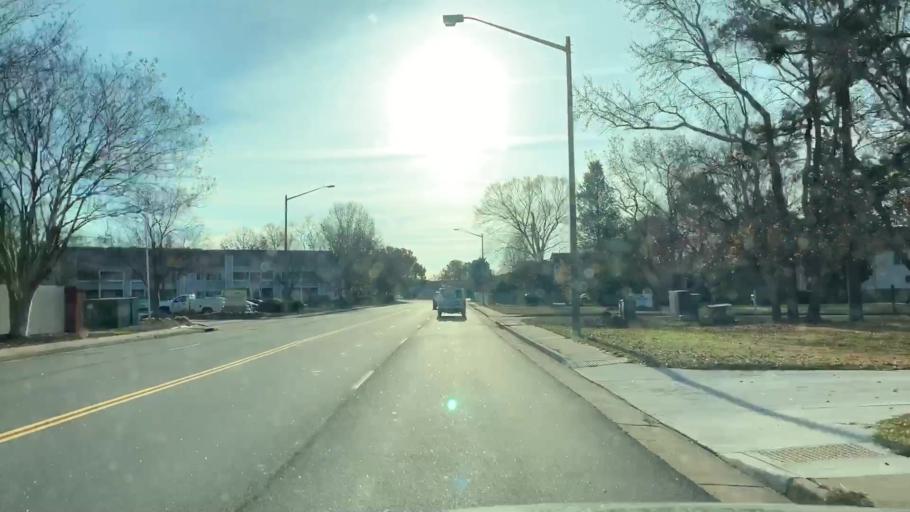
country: US
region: Virginia
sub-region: City of Chesapeake
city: Chesapeake
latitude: 36.7909
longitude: -76.1663
